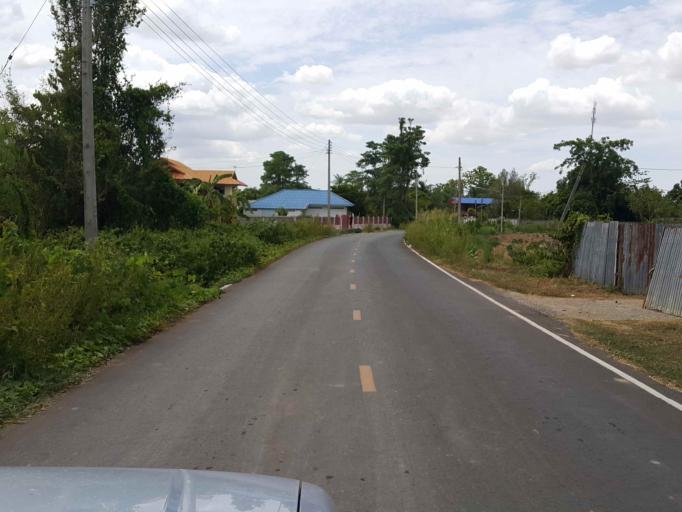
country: TH
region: Sukhothai
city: Thung Saliam
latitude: 17.3277
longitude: 99.5579
